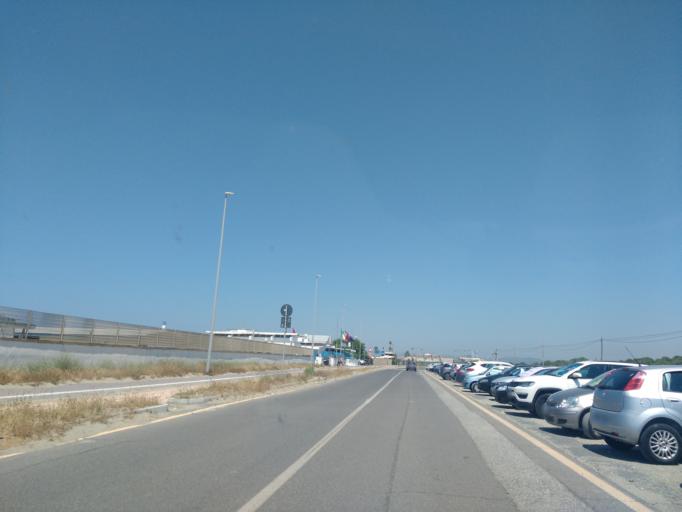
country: IT
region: Latium
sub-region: Citta metropolitana di Roma Capitale
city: Passo Oscuro
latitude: 41.8850
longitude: 12.1710
